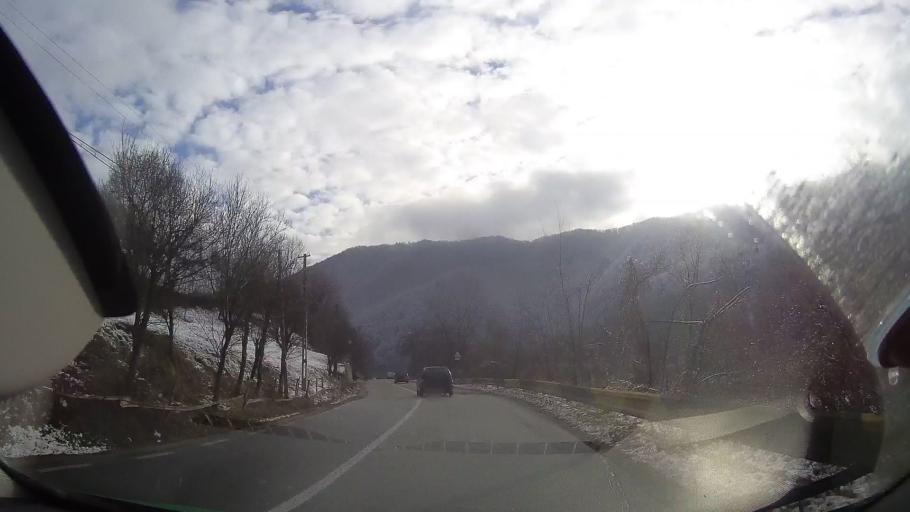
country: RO
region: Alba
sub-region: Oras Baia de Aries
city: Baia de Aries
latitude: 46.4000
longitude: 23.3100
